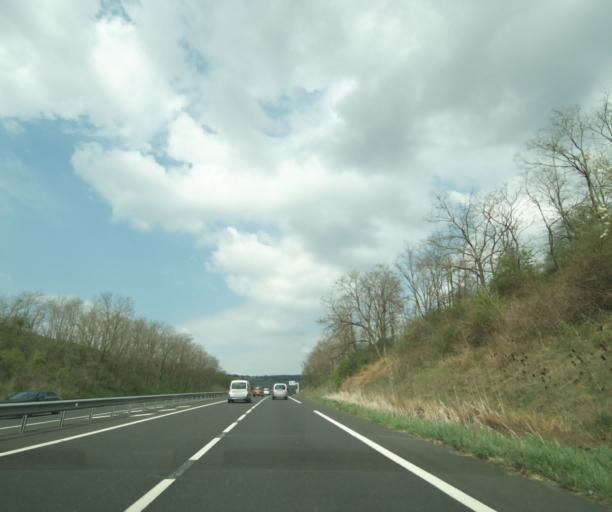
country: FR
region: Auvergne
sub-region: Departement du Puy-de-Dome
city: Le Breuil-sur-Couze
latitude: 45.4857
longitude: 3.2469
